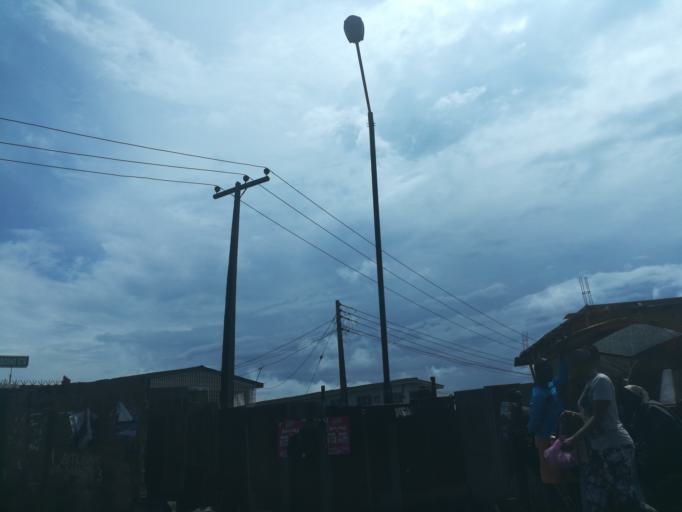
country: NG
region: Lagos
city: Agege
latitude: 6.6208
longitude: 3.3296
